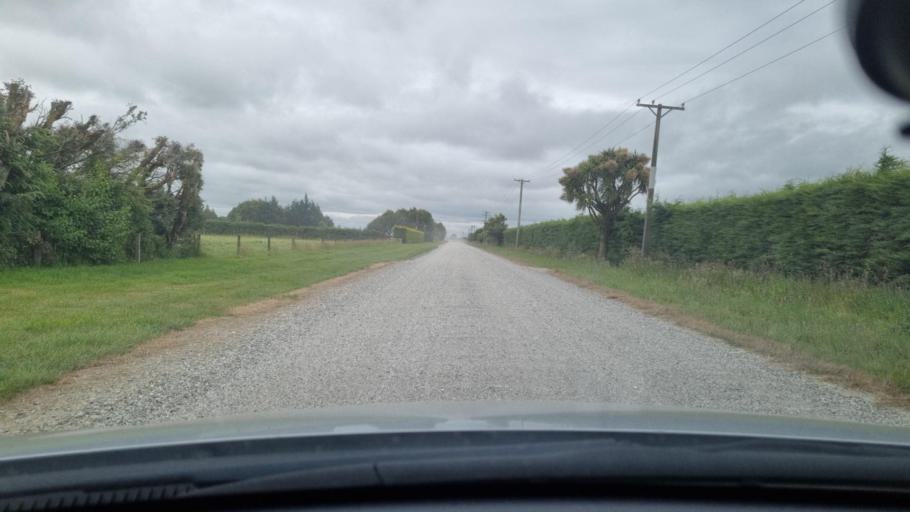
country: NZ
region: Southland
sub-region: Invercargill City
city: Invercargill
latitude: -46.3750
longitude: 168.2985
